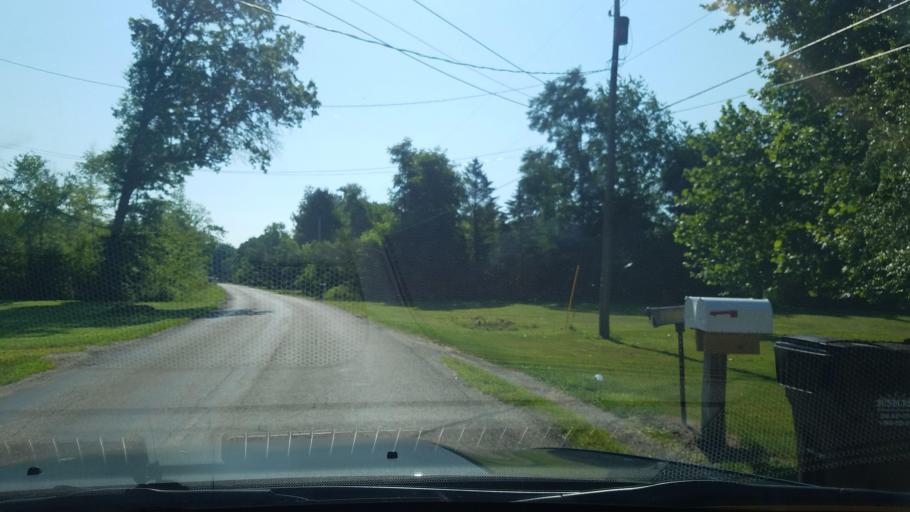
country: US
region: Ohio
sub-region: Trumbull County
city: Leavittsburg
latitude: 41.2589
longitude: -80.9091
